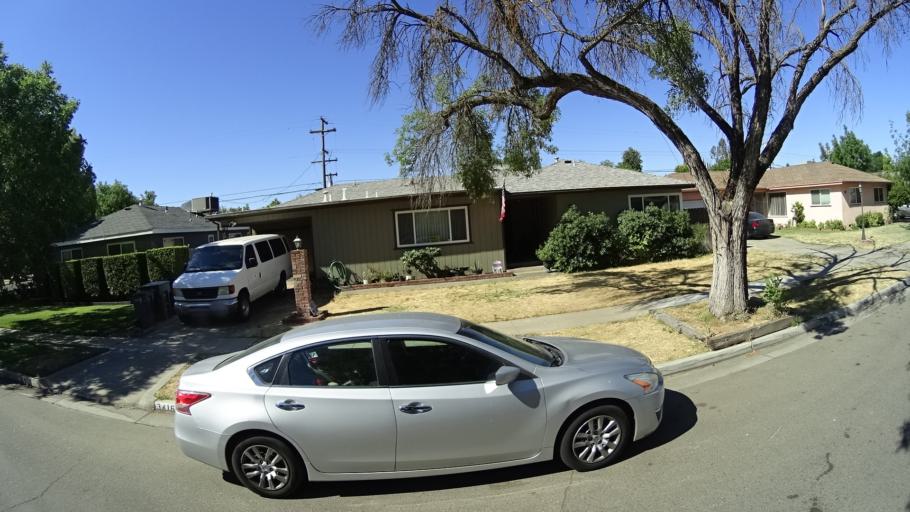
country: US
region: California
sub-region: Fresno County
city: Fresno
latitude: 36.7775
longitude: -119.7673
